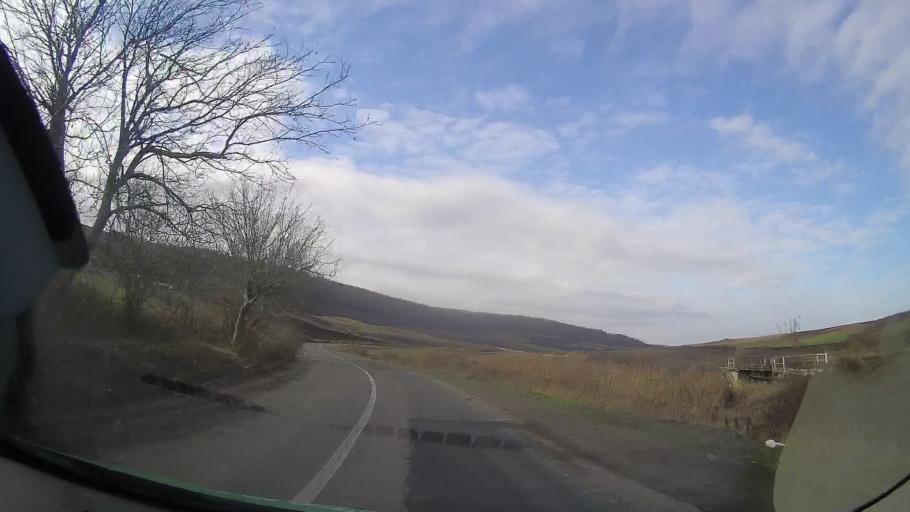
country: RO
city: Barza
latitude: 46.5533
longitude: 24.1100
